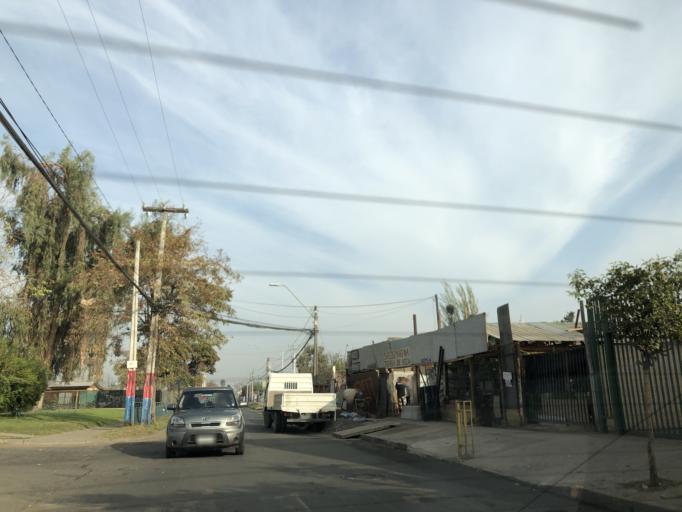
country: CL
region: Santiago Metropolitan
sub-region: Provincia de Cordillera
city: Puente Alto
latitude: -33.5888
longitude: -70.5714
